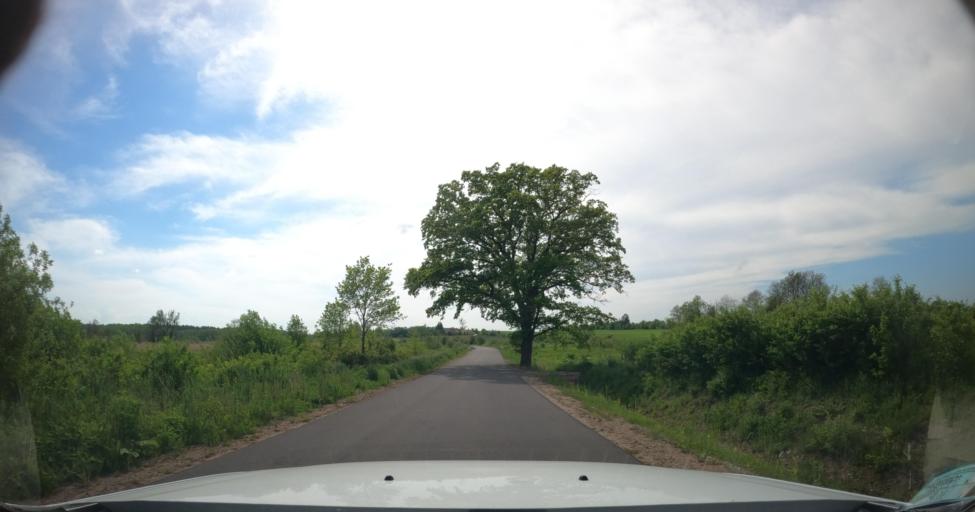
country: PL
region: Warmian-Masurian Voivodeship
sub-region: Powiat lidzbarski
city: Lidzbark Warminski
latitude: 54.1236
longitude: 20.5288
